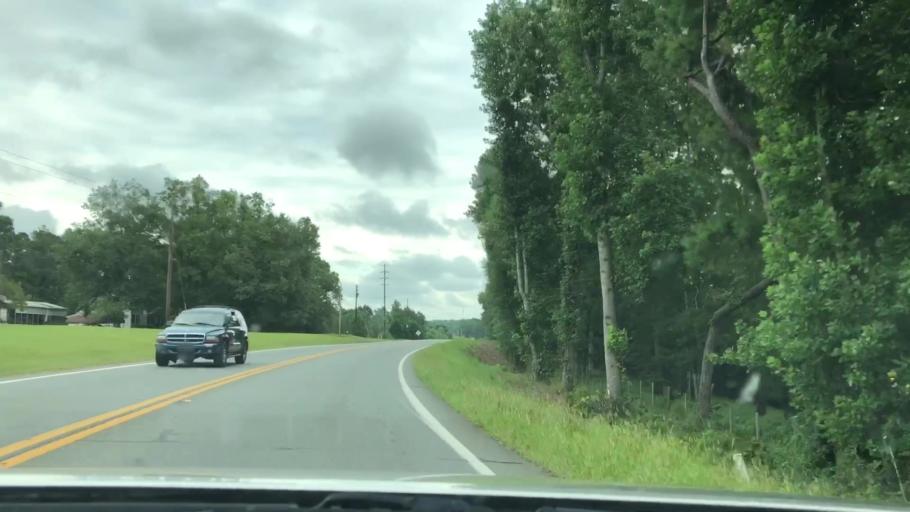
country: US
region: Georgia
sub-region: Pike County
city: Zebulon
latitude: 33.1077
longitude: -84.3664
